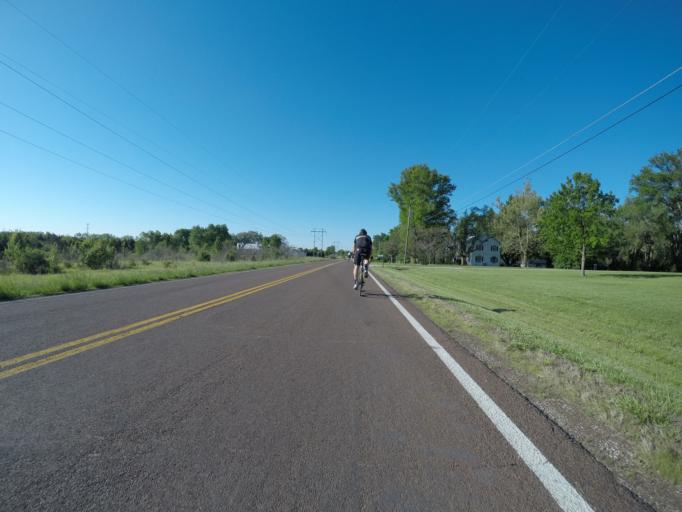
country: US
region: Kansas
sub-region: Shawnee County
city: Topeka
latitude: 39.0470
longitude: -95.5665
